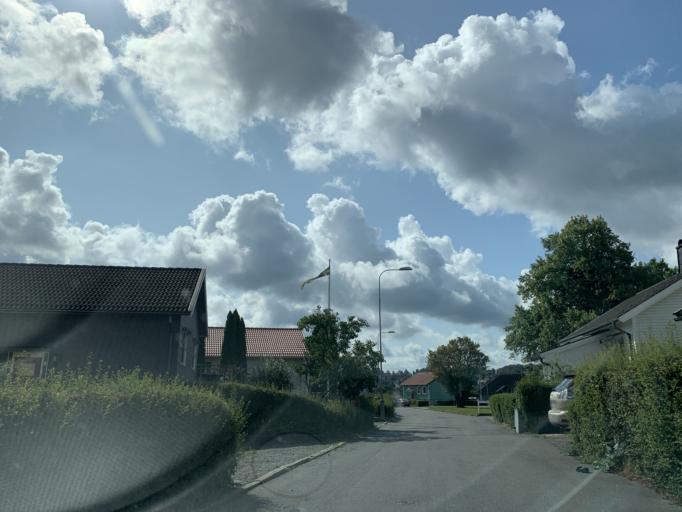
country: SE
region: Vaestra Goetaland
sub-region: Goteborg
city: Eriksbo
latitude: 57.7403
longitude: 12.0661
